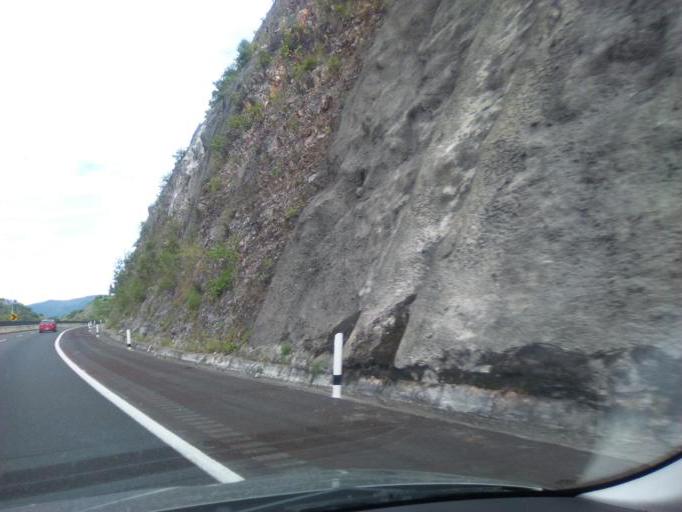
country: MX
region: Guerrero
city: Huitziltepec
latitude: 17.7333
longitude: -99.5002
